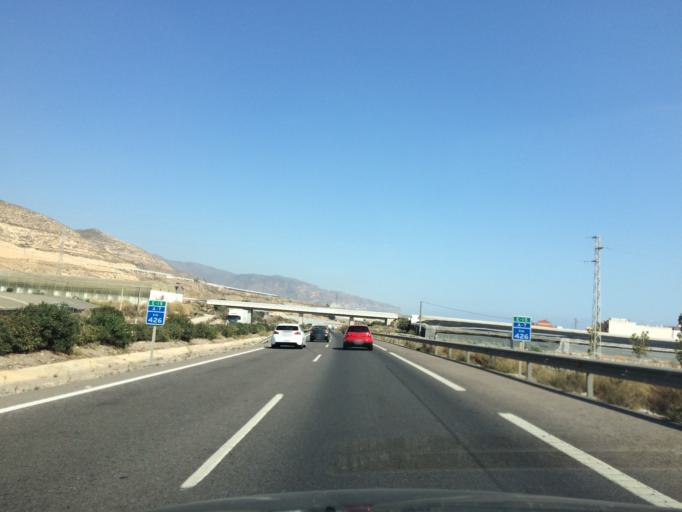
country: ES
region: Andalusia
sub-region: Provincia de Almeria
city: Vicar
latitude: 36.8109
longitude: -2.6322
